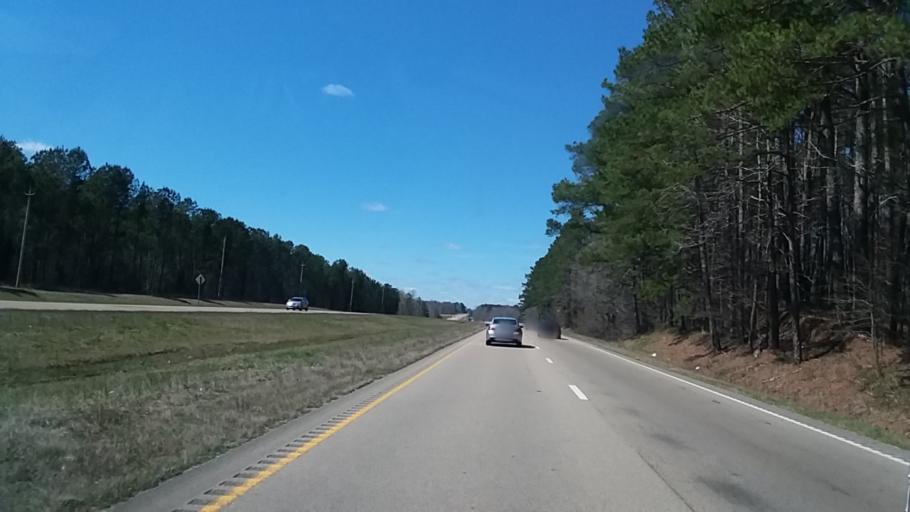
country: US
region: Mississippi
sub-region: Alcorn County
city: Farmington
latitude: 34.8859
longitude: -88.4538
